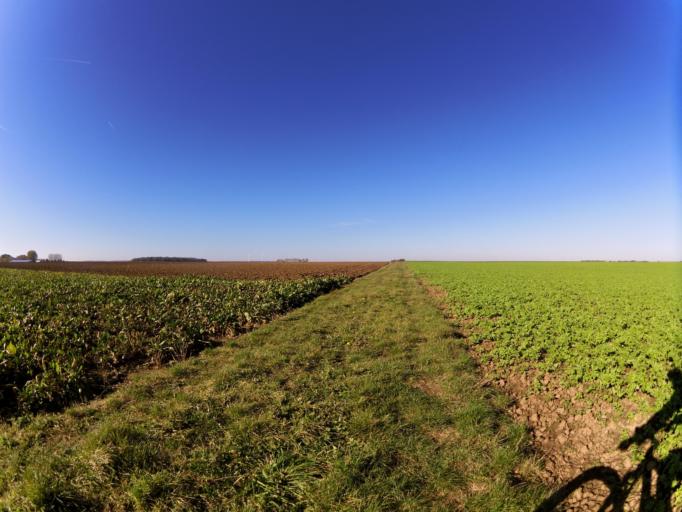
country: DE
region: Bavaria
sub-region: Regierungsbezirk Unterfranken
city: Giebelstadt
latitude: 49.6617
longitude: 9.9387
